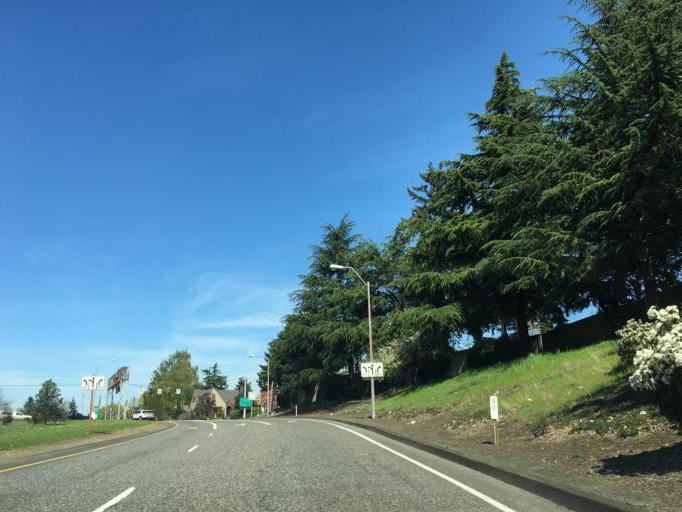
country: US
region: Oregon
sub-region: Multnomah County
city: Portland
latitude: 45.5689
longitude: -122.6780
